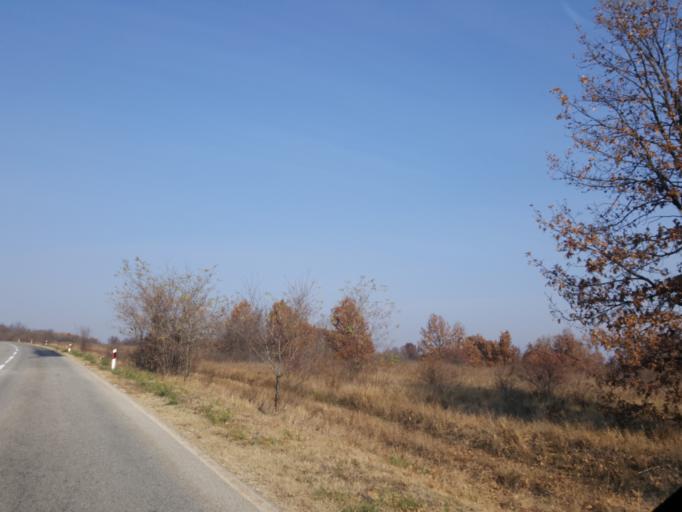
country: RS
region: Central Serbia
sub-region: Zajecarski Okrug
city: Zajecar
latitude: 44.0530
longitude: 22.3349
